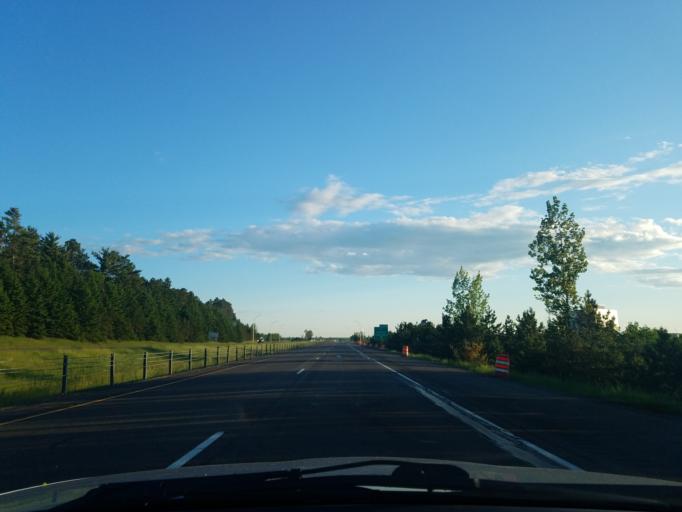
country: US
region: Minnesota
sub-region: Carlton County
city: Carlton
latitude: 46.6681
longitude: -92.4717
